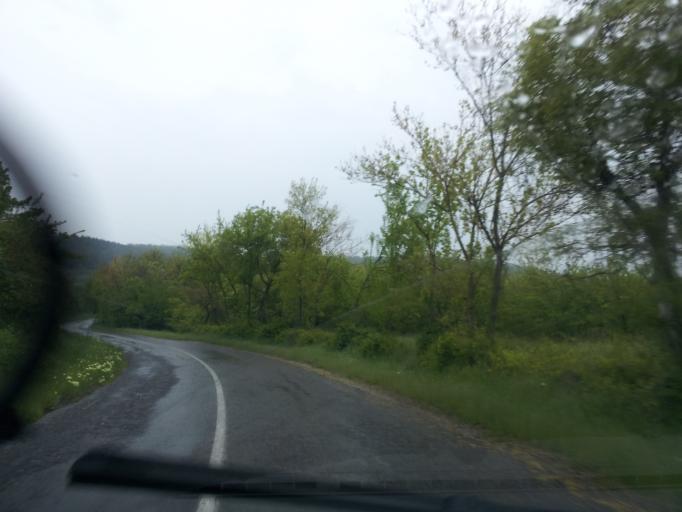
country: HU
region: Tolna
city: Szekszard
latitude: 46.2931
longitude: 18.6775
